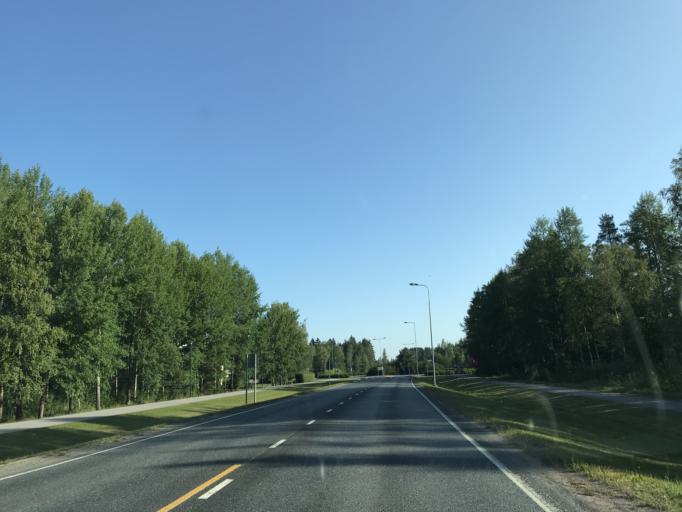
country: FI
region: Paijanne Tavastia
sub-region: Lahti
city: Orimattila
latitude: 60.8087
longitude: 25.7288
